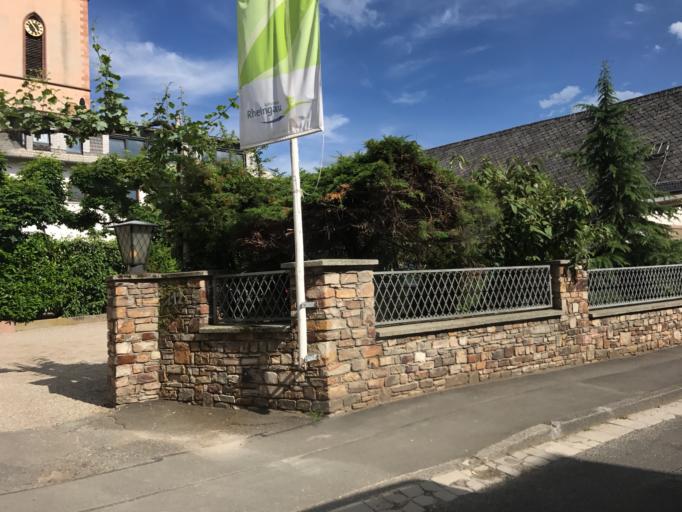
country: DE
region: Hesse
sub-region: Regierungsbezirk Darmstadt
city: Eltville
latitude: 50.0594
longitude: 8.1106
